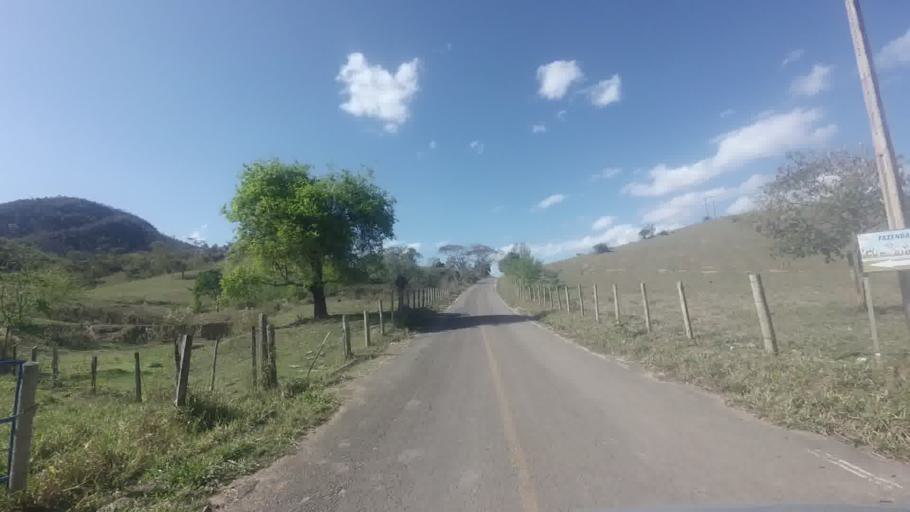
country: BR
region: Rio de Janeiro
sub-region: Bom Jesus Do Itabapoana
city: Bom Jesus do Itabapoana
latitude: -21.1149
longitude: -41.6521
